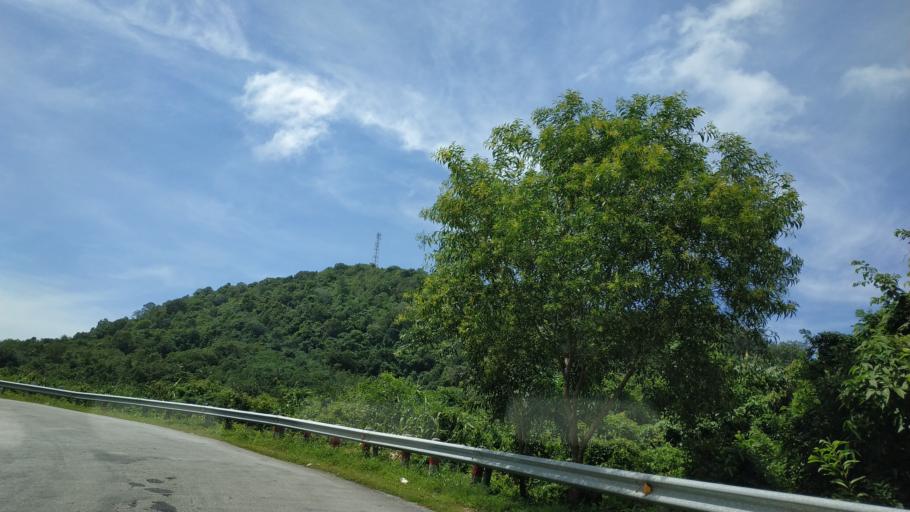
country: MM
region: Tanintharyi
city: Dawei
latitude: 14.1435
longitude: 98.1128
